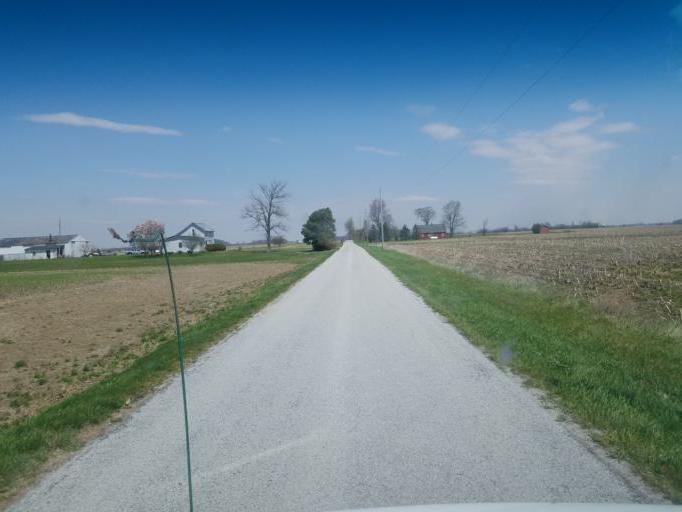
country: US
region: Ohio
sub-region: Hardin County
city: Kenton
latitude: 40.6948
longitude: -83.5473
